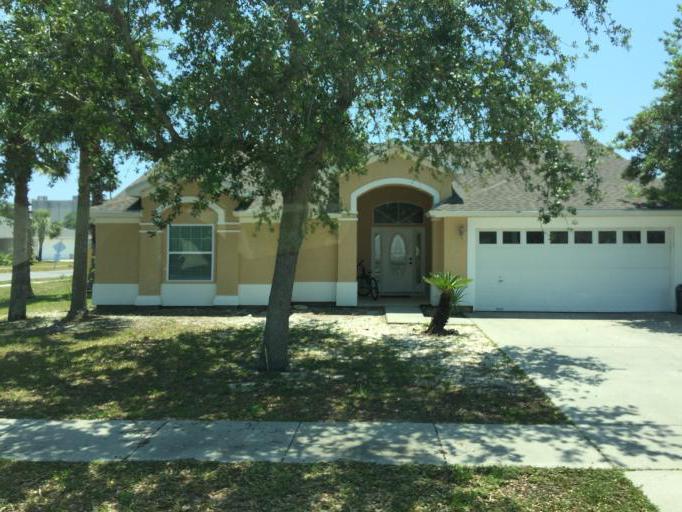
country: US
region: Florida
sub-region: Bay County
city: Panama City Beach
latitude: 30.2140
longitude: -85.8592
